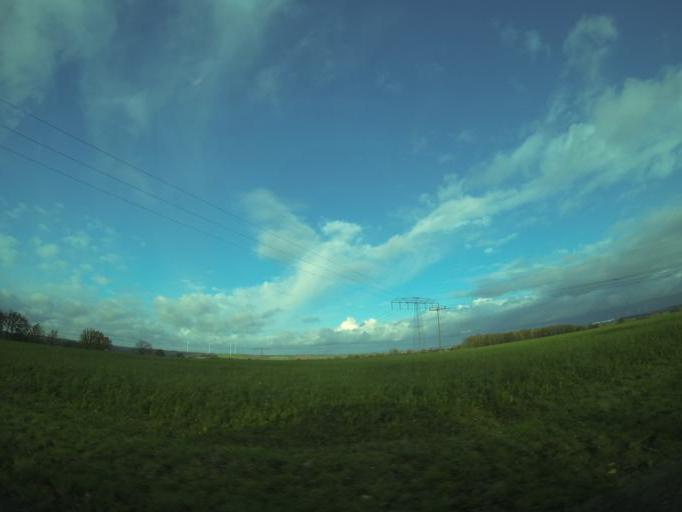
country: DE
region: Thuringia
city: Nobdenitz
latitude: 50.8671
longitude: 12.2954
